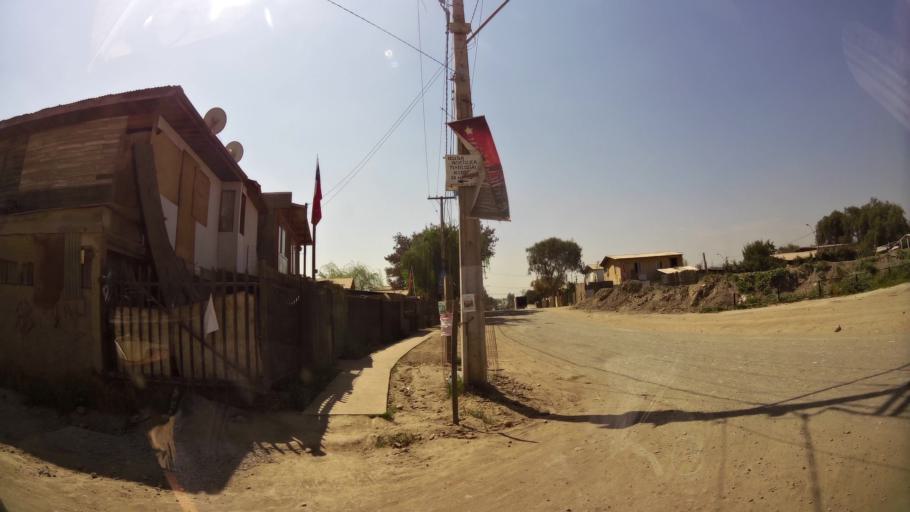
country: CL
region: Santiago Metropolitan
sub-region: Provincia de Talagante
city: Penaflor
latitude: -33.5837
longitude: -70.8124
